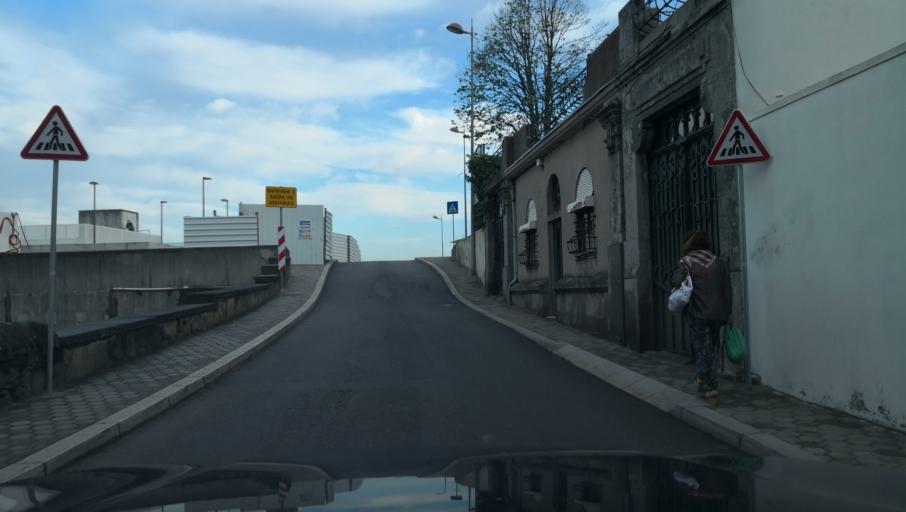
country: PT
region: Porto
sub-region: Vila Nova de Gaia
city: Vila Nova de Gaia
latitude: 41.1329
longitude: -8.6081
